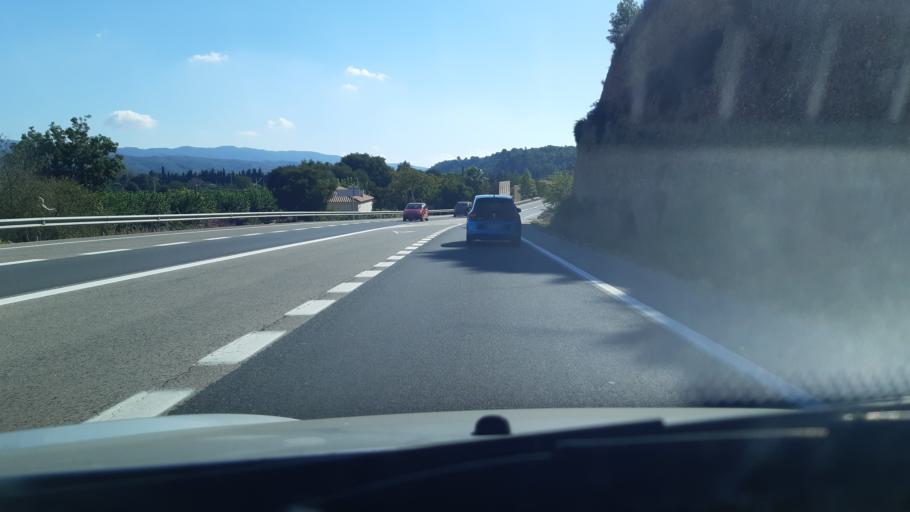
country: ES
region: Catalonia
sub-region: Provincia de Tarragona
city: Tivenys
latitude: 40.8764
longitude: 0.5005
